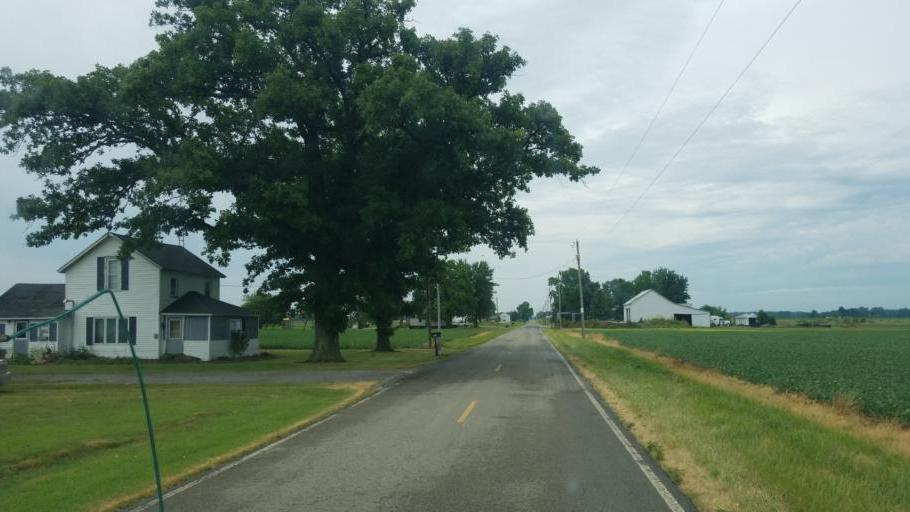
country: US
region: Ohio
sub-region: Defiance County
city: Hicksville
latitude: 41.2776
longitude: -84.6895
